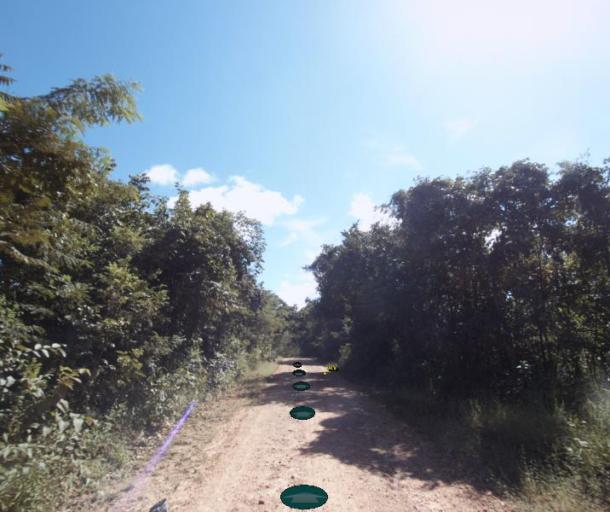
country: BR
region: Goias
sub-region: Pirenopolis
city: Pirenopolis
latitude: -15.7744
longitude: -49.0266
